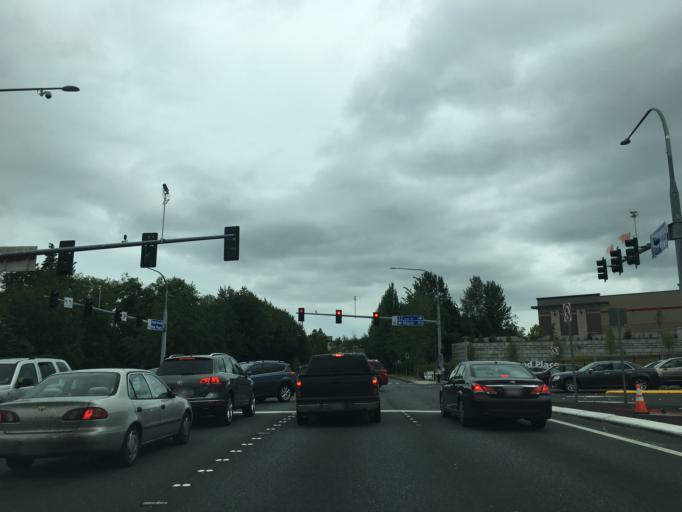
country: US
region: Washington
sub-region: Snohomish County
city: Alderwood Manor
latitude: 47.8362
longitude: -122.2720
